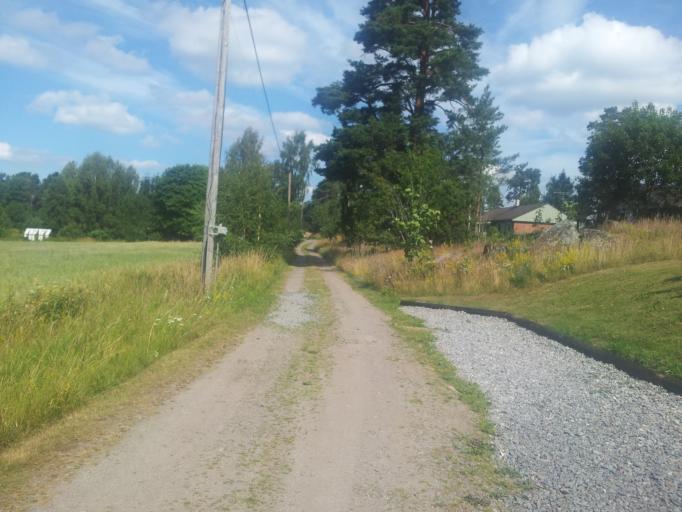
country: SE
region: Stockholm
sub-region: Norrtalje Kommun
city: Nykvarn
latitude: 59.8902
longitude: 18.2287
